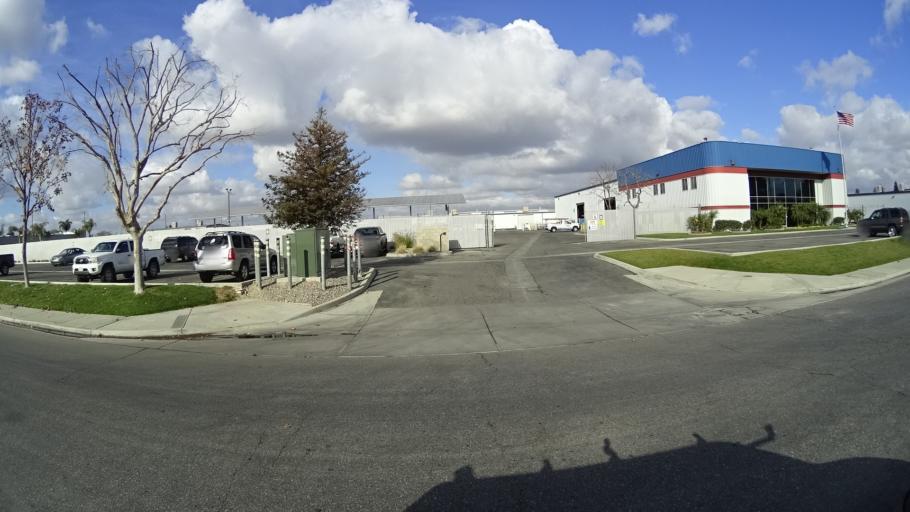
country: US
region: California
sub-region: Kern County
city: Bakersfield
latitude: 35.3469
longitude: -118.9696
